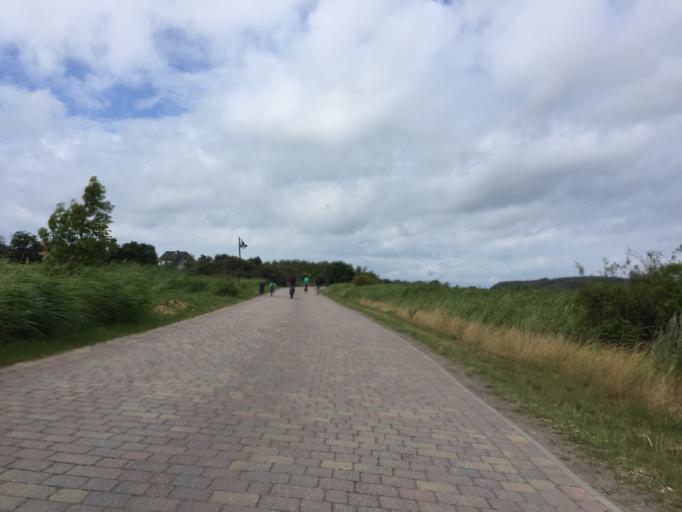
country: DE
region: Mecklenburg-Vorpommern
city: Hiddensee
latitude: 54.5739
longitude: 13.1061
